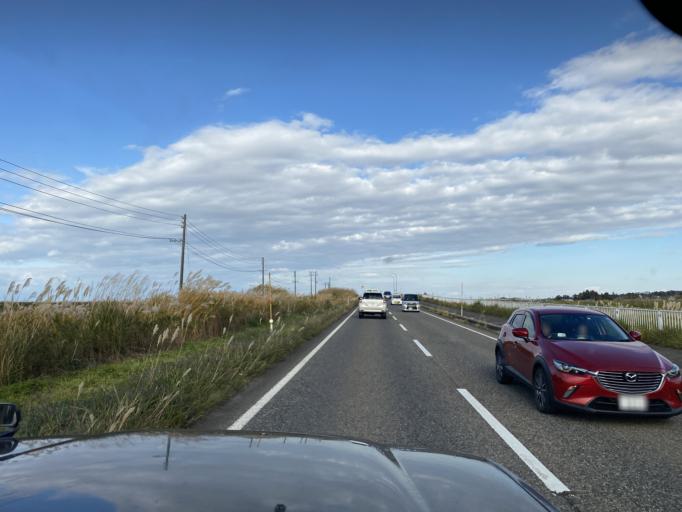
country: JP
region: Niigata
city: Niitsu-honcho
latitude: 37.7753
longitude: 139.1059
